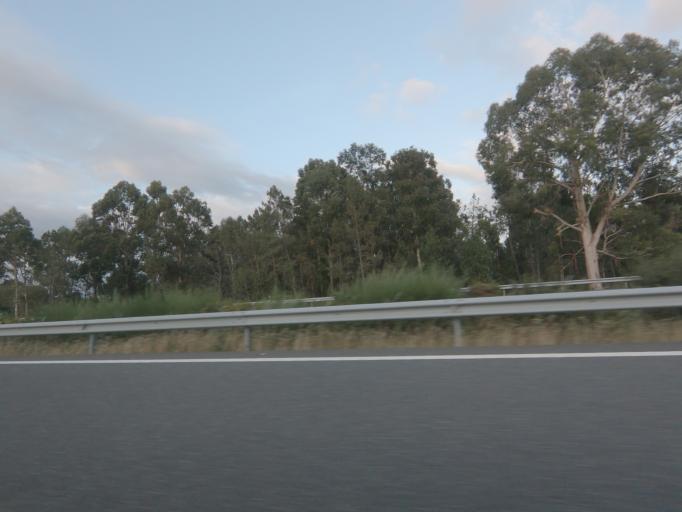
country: ES
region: Galicia
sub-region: Provincia de Ourense
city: Melon
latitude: 42.2083
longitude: -8.2653
